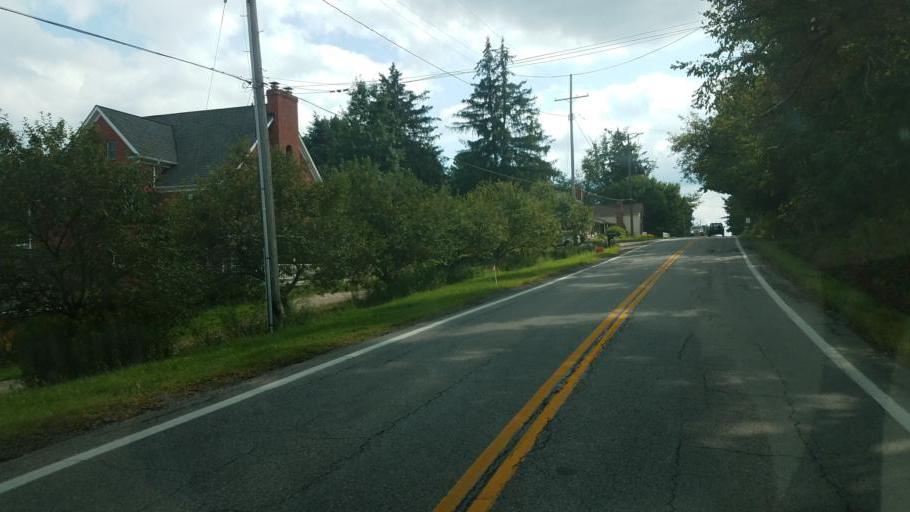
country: US
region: Ohio
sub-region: Geauga County
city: Burton
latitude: 41.4399
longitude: -81.2076
